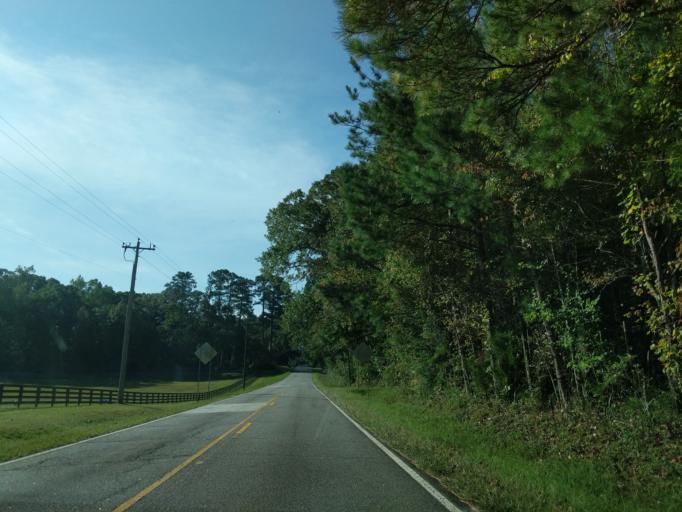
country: US
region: Georgia
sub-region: Coweta County
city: Newnan
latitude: 33.3498
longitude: -84.9185
